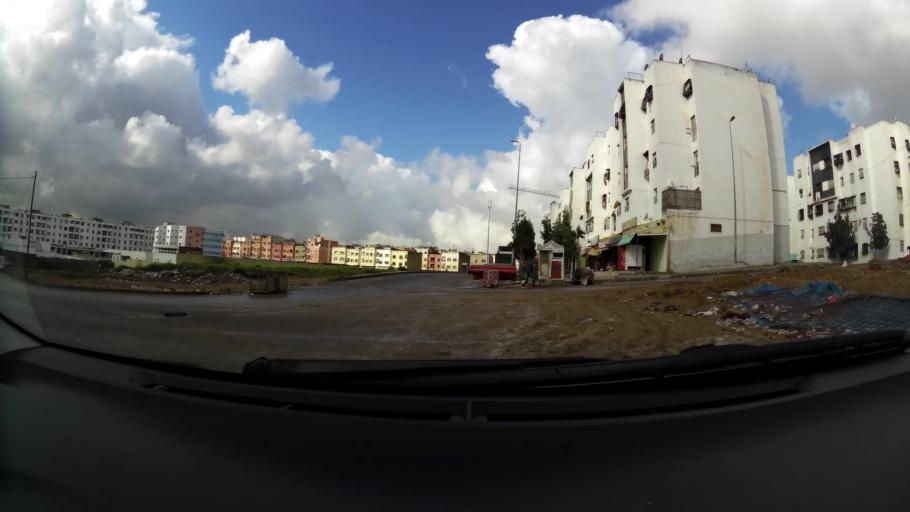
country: MA
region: Grand Casablanca
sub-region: Mediouna
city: Tit Mellil
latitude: 33.5766
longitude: -7.5244
